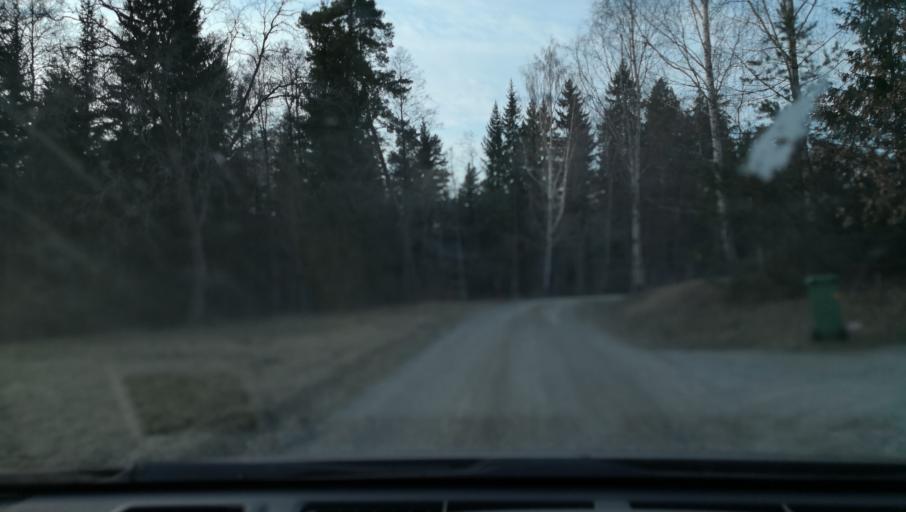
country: SE
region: OErebro
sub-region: Lindesbergs Kommun
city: Frovi
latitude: 59.3503
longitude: 15.3428
